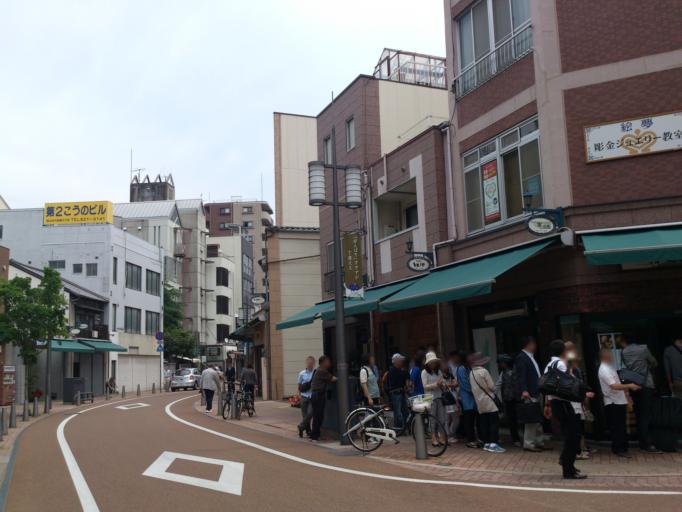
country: JP
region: Ehime
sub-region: Shikoku-chuo Shi
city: Matsuyama
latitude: 33.8416
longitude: 132.7702
